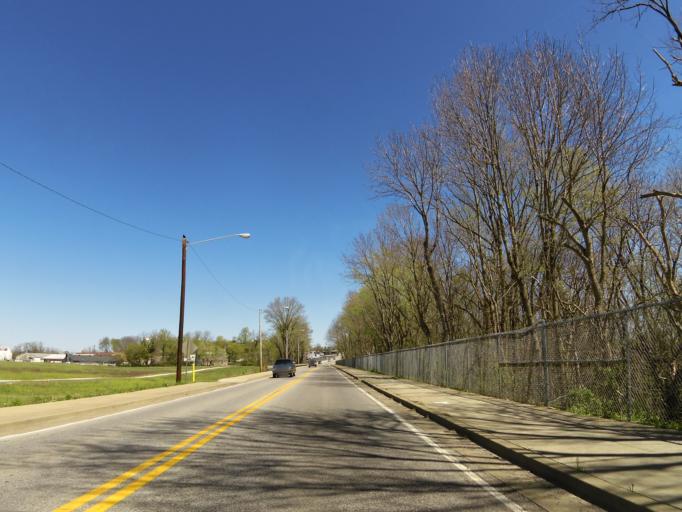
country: US
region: Kentucky
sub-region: Warren County
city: Bowling Green
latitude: 37.0014
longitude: -86.4273
